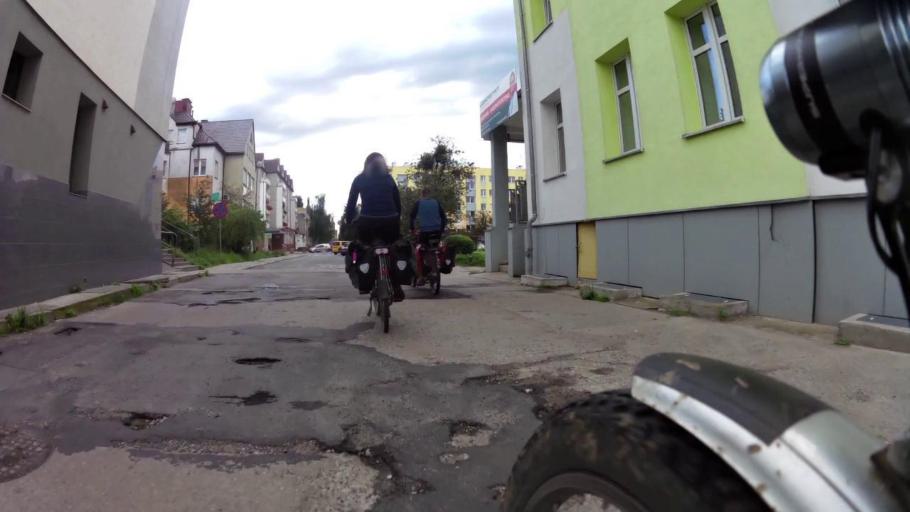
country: PL
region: West Pomeranian Voivodeship
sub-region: Powiat gryfinski
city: Gryfino
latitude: 53.2548
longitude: 14.4899
